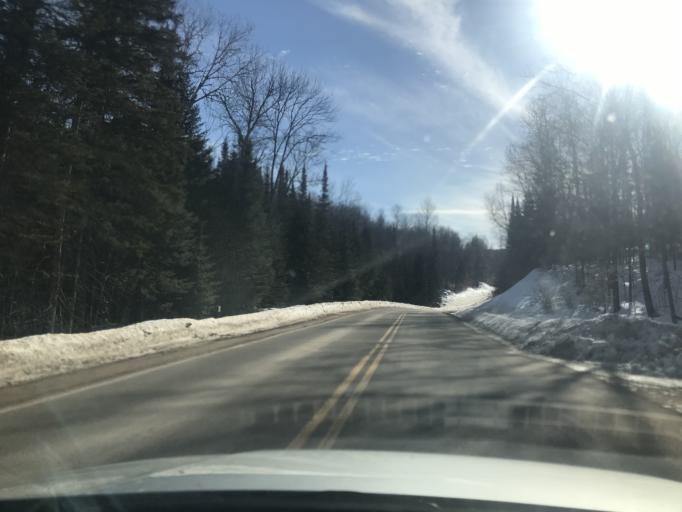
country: US
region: Michigan
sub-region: Dickinson County
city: Kingsford
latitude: 45.4123
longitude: -88.3915
